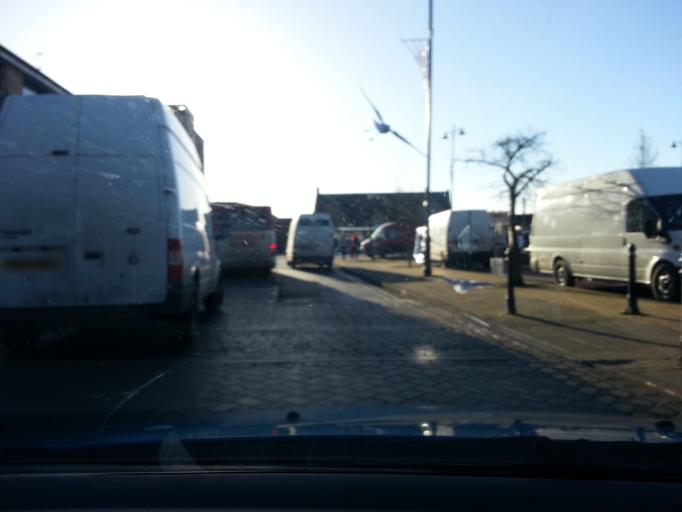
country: GB
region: England
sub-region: County Durham
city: Crook
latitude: 54.7145
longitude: -1.7454
